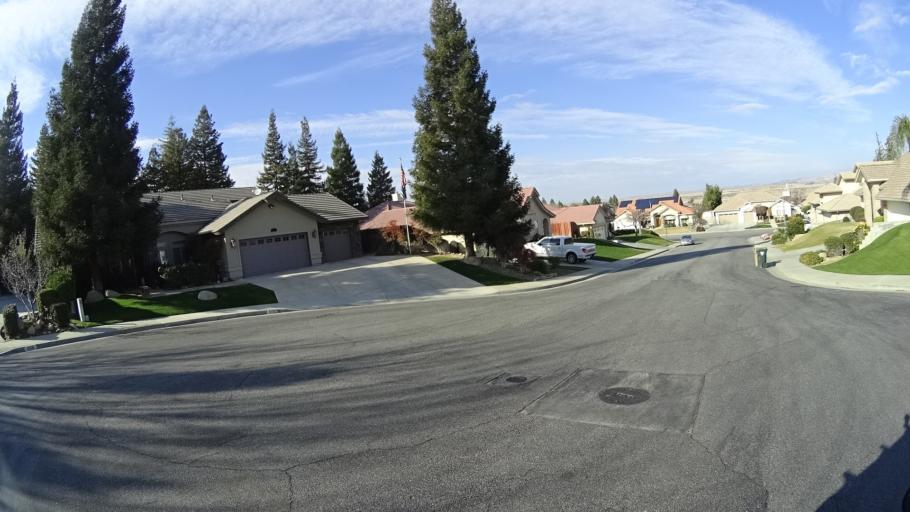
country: US
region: California
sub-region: Kern County
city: Oildale
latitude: 35.4005
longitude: -118.9148
